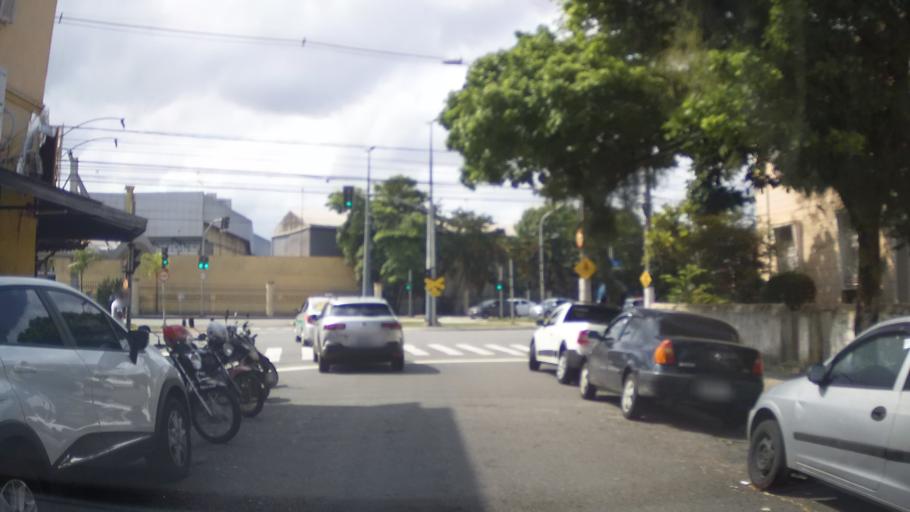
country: BR
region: Sao Paulo
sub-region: Santos
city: Santos
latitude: -23.9604
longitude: -46.3346
